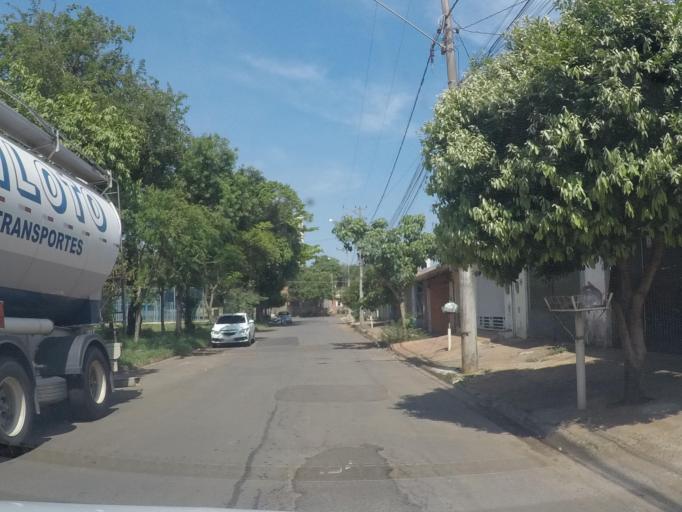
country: BR
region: Sao Paulo
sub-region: Sumare
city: Sumare
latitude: -22.8398
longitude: -47.2707
